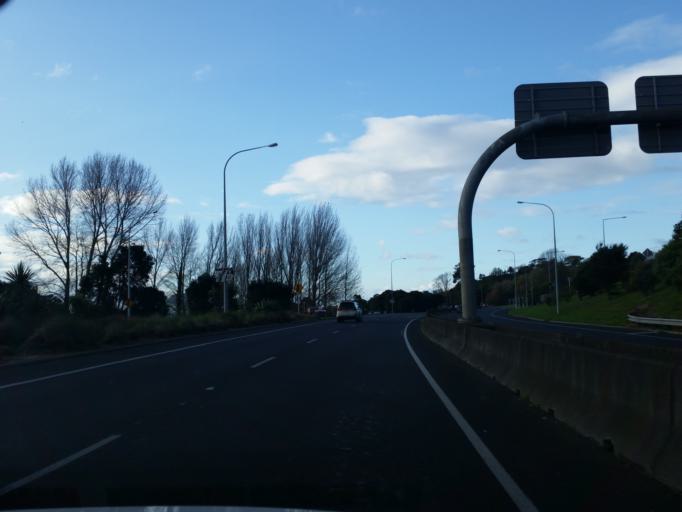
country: NZ
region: Bay of Plenty
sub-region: Tauranga City
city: Tauranga
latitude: -37.6970
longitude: 176.1539
